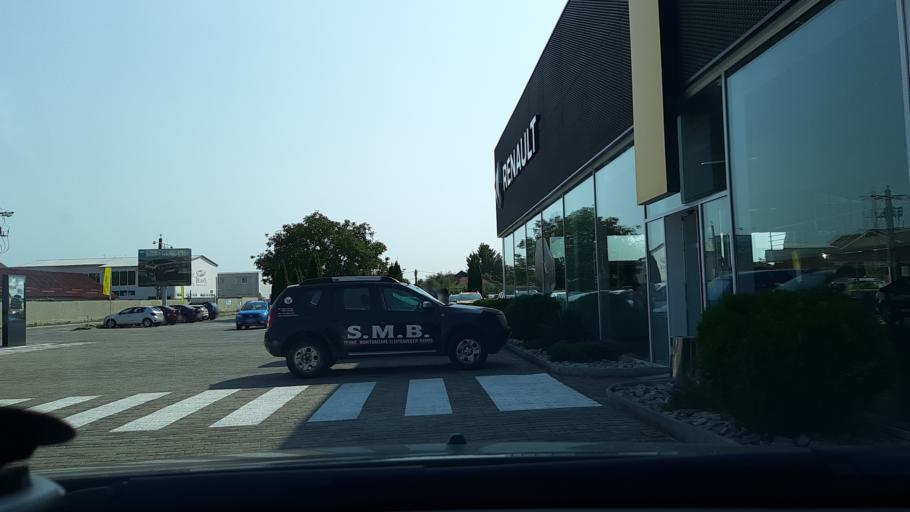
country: RO
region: Gorj
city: Targu Jiu
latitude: 45.0166
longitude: 23.2650
